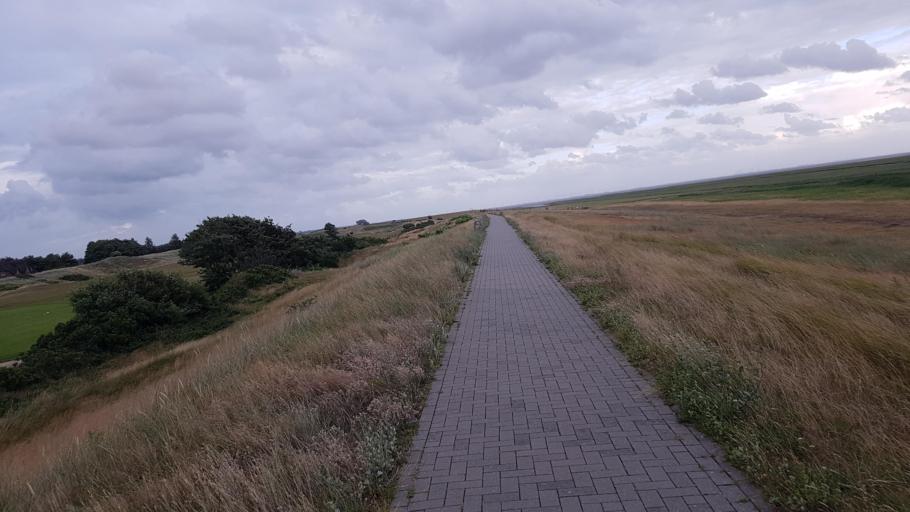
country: DE
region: Schleswig-Holstein
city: Sankt Peter-Ording
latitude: 54.2801
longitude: 8.6702
